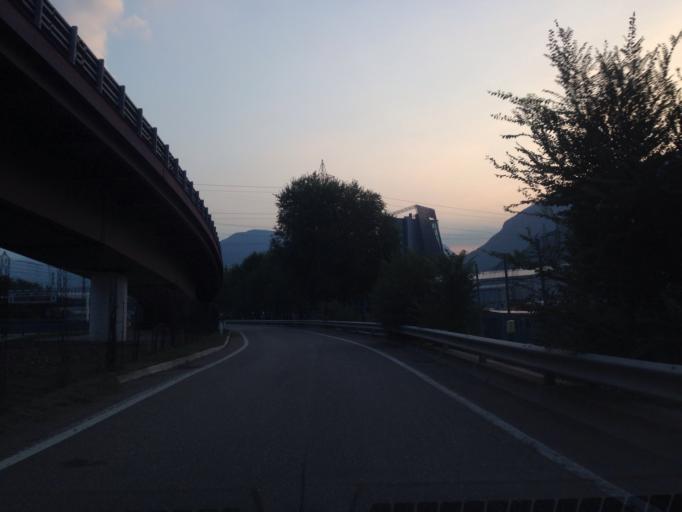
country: IT
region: Trentino-Alto Adige
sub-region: Bolzano
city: San Giacomo
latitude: 46.4746
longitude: 11.3203
